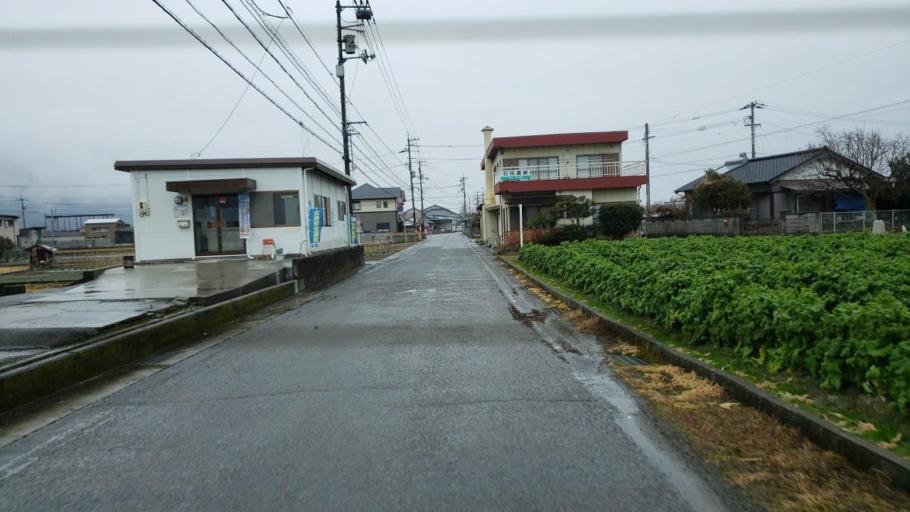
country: JP
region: Tokushima
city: Kamojimacho-jogejima
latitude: 34.0589
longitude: 134.2950
